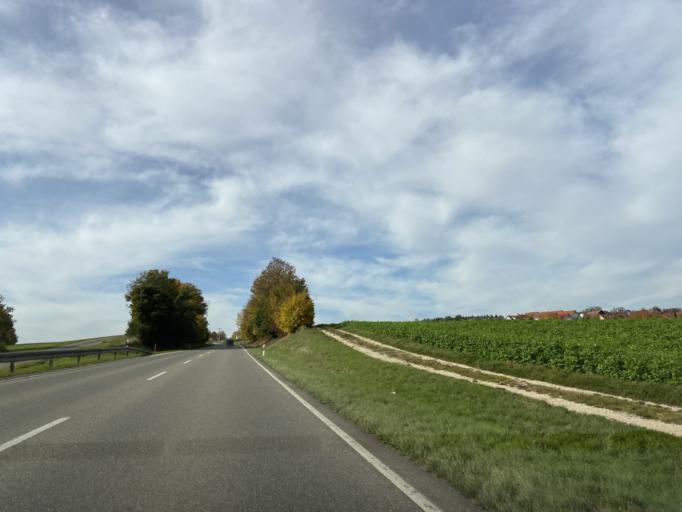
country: DE
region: Baden-Wuerttemberg
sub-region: Tuebingen Region
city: Inzigkofen
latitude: 48.0672
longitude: 9.1749
